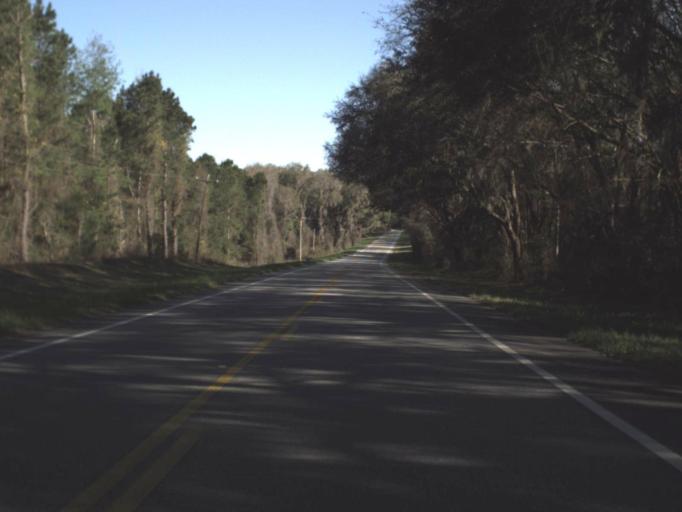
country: US
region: Georgia
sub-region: Brooks County
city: Quitman
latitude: 30.5698
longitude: -83.6373
